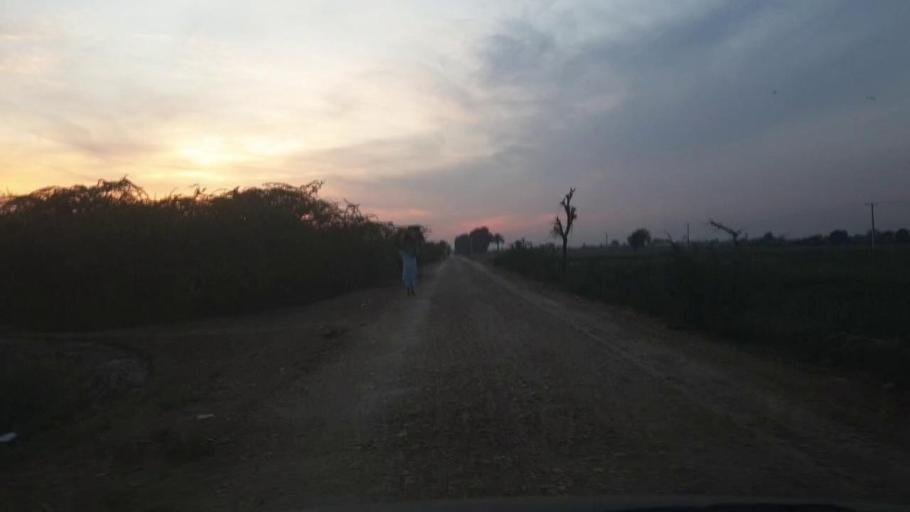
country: PK
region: Sindh
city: Kunri
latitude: 25.2240
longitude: 69.5315
